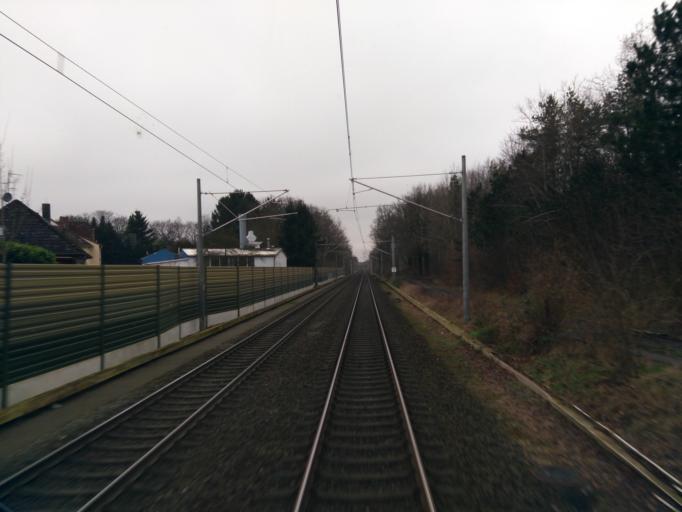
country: DE
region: Hamburg
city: Harburg
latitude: 53.4275
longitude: 10.0171
